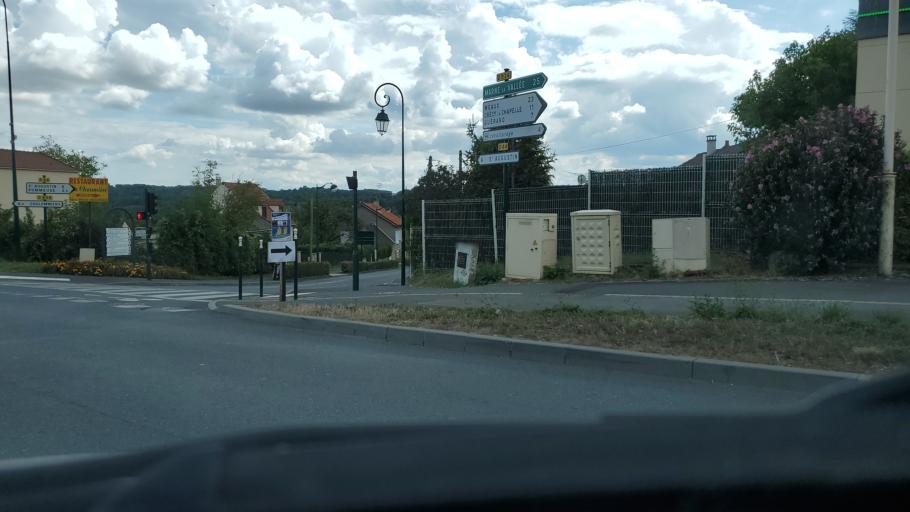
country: FR
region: Ile-de-France
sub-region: Departement de Seine-et-Marne
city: Mouroux
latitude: 48.8255
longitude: 3.0377
